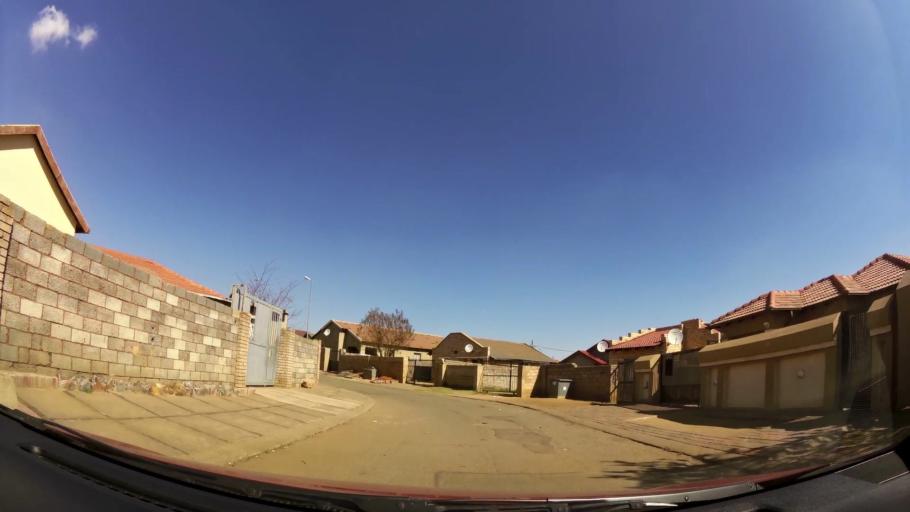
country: ZA
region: Gauteng
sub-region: City of Johannesburg Metropolitan Municipality
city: Soweto
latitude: -26.2394
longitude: 27.8168
